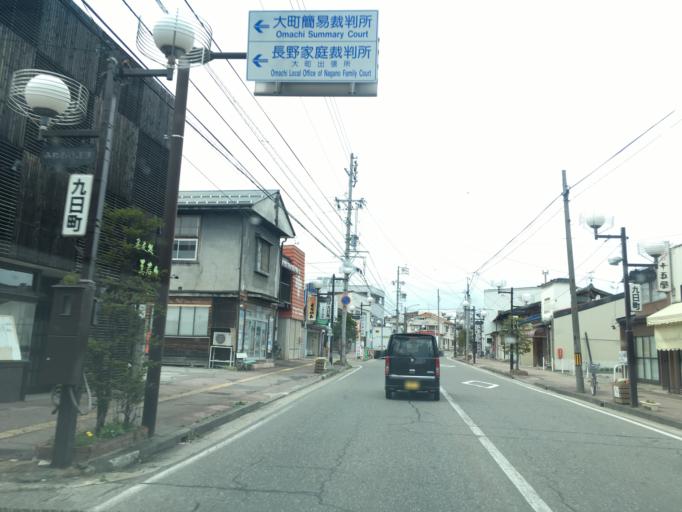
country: JP
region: Nagano
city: Omachi
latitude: 36.5085
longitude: 137.8578
